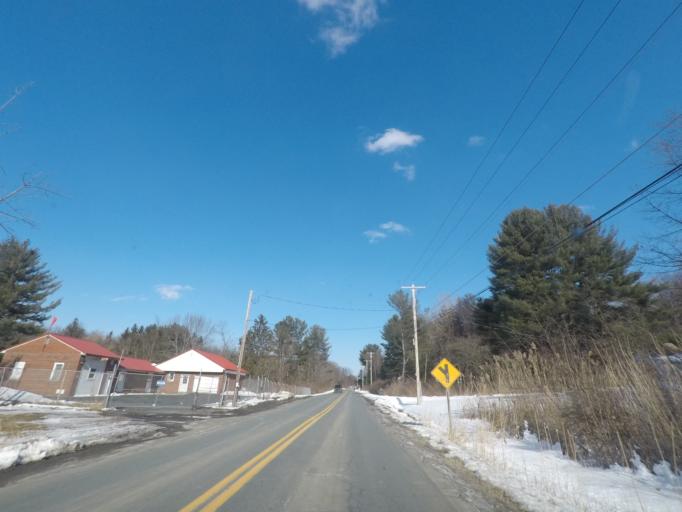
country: US
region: New York
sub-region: Saratoga County
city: Waterford
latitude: 42.8496
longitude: -73.6099
